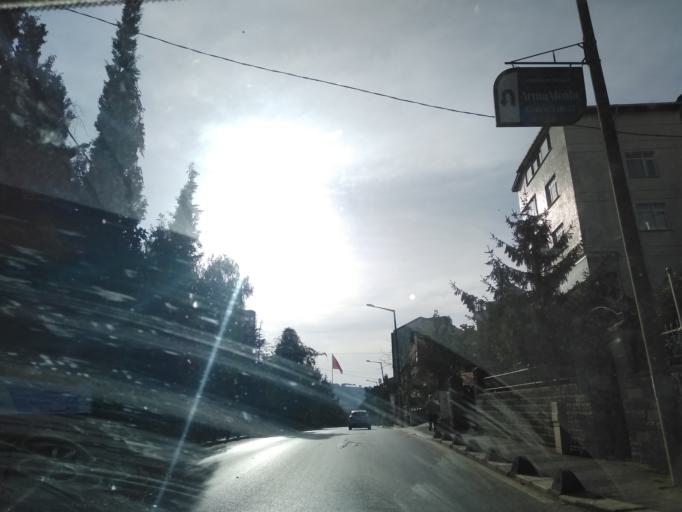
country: TR
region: Istanbul
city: Maltepe
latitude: 40.9171
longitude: 29.1580
